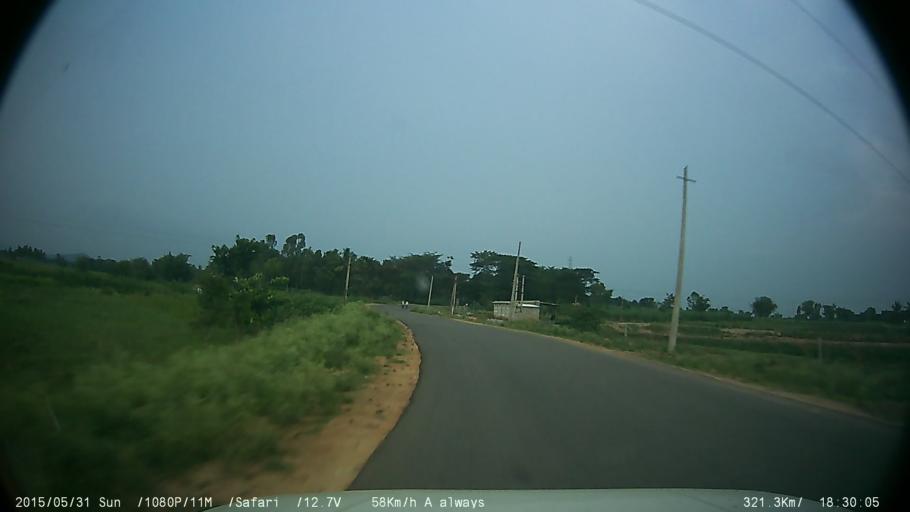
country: IN
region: Karnataka
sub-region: Mysore
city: Nanjangud
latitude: 12.1236
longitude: 76.7361
